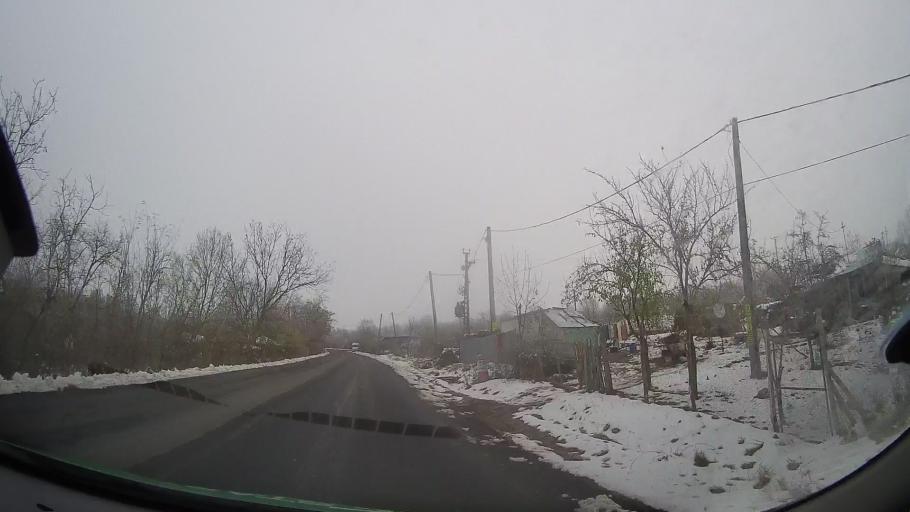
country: RO
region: Bacau
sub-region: Comuna Podu Turcului
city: Podu Turcului
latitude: 46.2086
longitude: 27.4409
